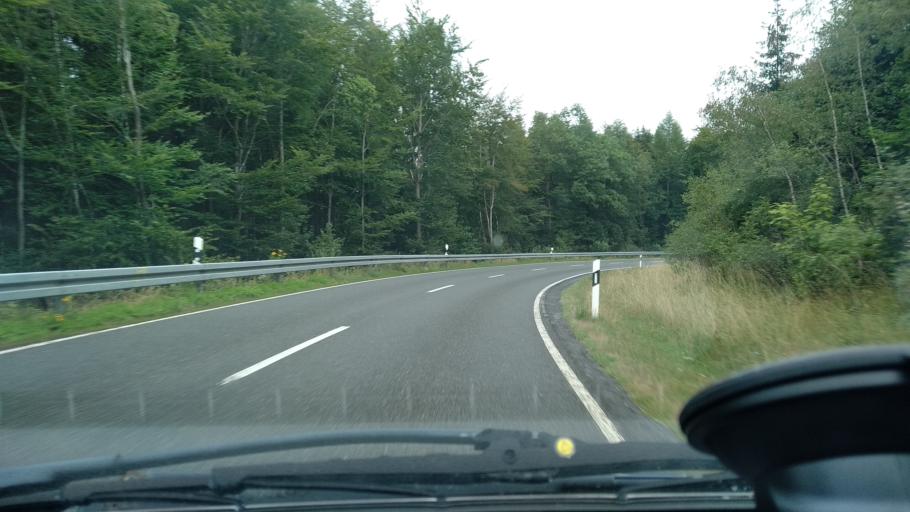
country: DE
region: Hesse
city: Dillenburg
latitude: 50.8512
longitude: 8.2533
